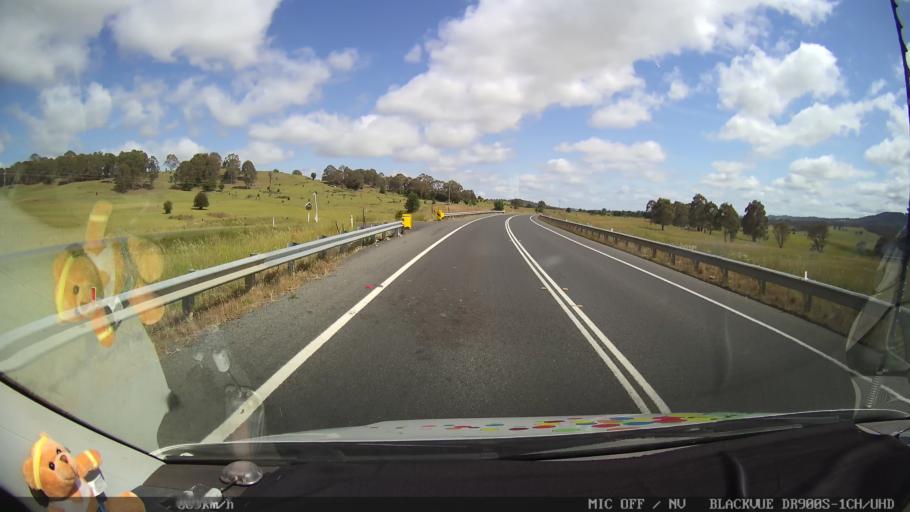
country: AU
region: New South Wales
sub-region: Glen Innes Severn
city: Glen Innes
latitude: -29.8909
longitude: 151.7338
